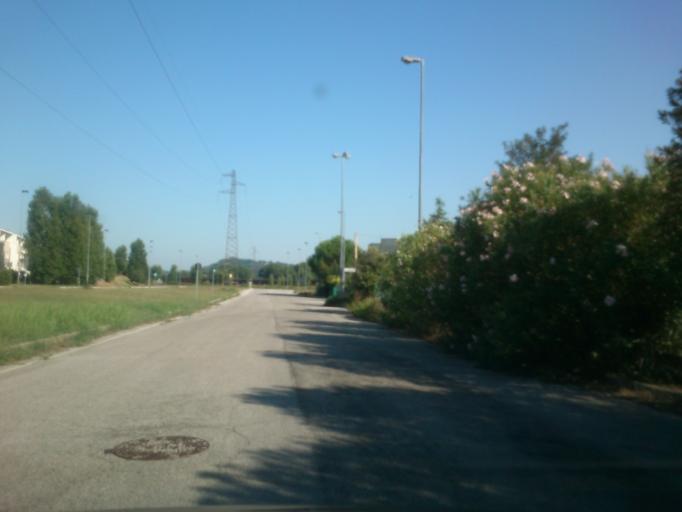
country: IT
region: The Marches
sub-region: Provincia di Pesaro e Urbino
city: Pesaro
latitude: 43.9014
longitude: 12.8579
